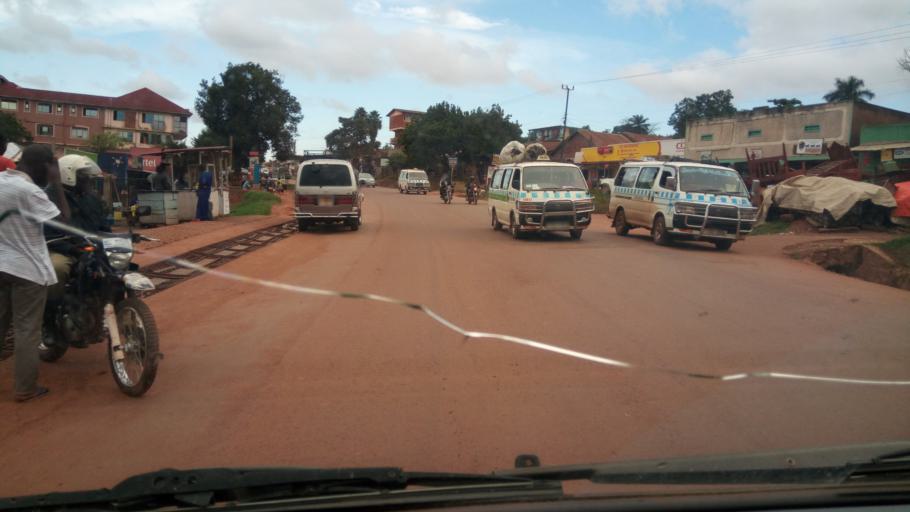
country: UG
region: Central Region
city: Kampala Central Division
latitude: 0.3333
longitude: 32.5498
